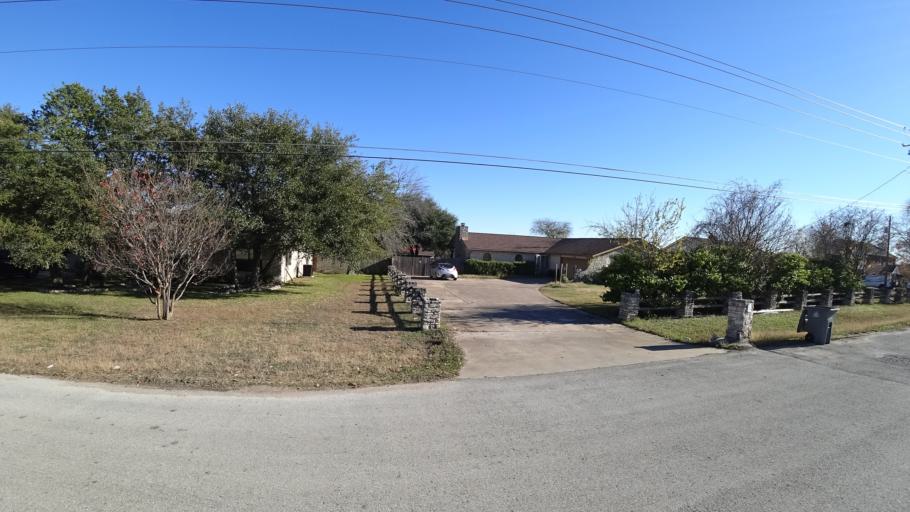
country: US
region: Texas
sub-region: Travis County
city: Wells Branch
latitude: 30.4071
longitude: -97.6923
